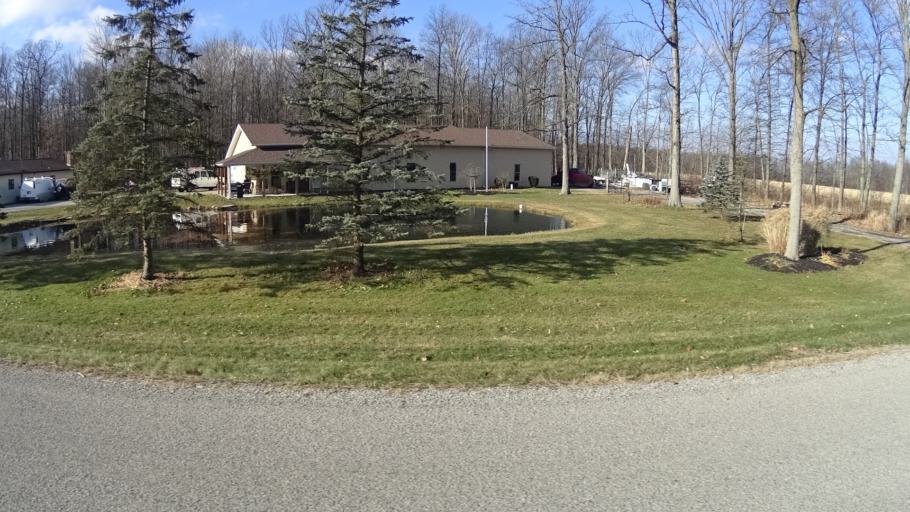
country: US
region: Ohio
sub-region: Lorain County
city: Wellington
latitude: 41.2302
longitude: -82.2364
